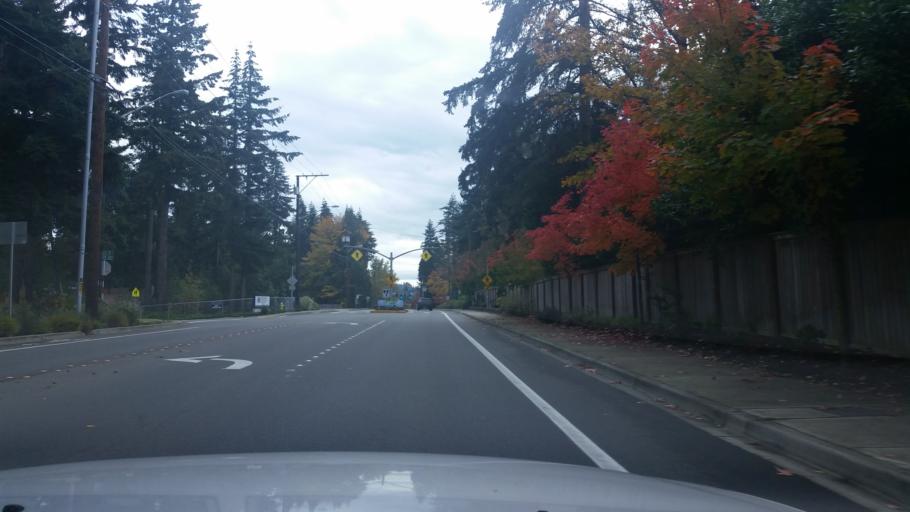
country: US
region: Washington
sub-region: King County
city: Eastgate
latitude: 47.5913
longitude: -122.1470
